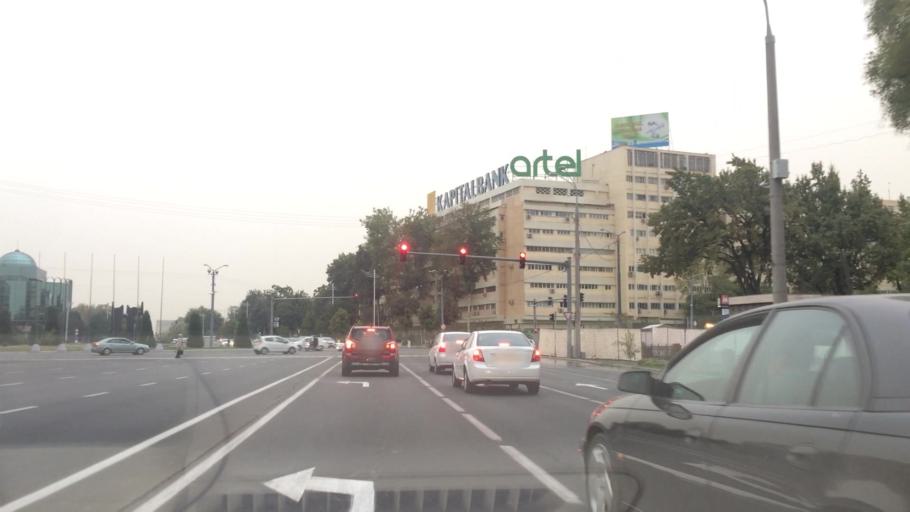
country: UZ
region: Toshkent Shahri
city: Tashkent
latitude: 41.3046
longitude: 69.2665
